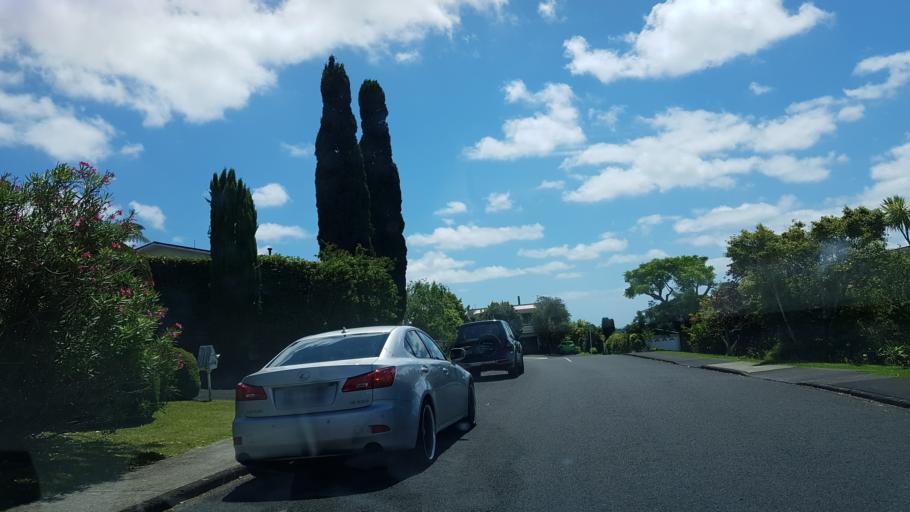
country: NZ
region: Auckland
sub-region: Auckland
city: North Shore
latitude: -36.7876
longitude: 174.7253
